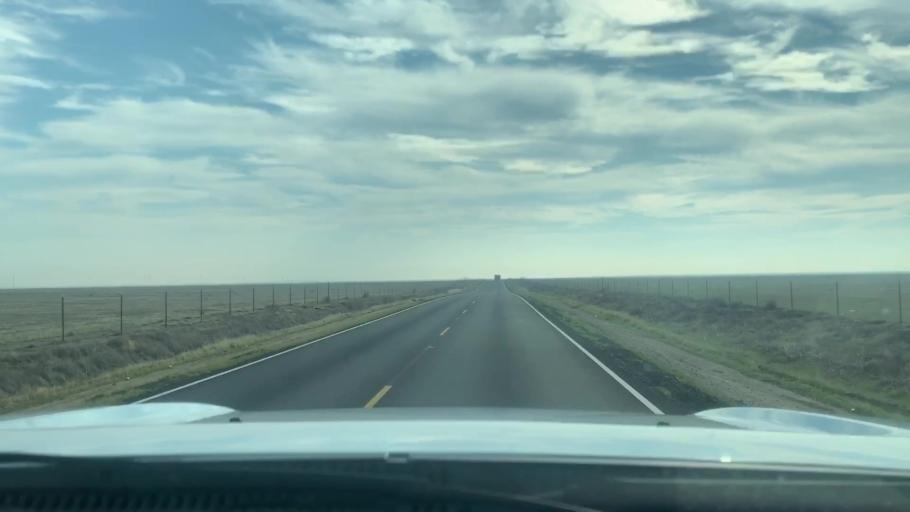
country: US
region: California
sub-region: Kern County
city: Lost Hills
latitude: 35.6064
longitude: -119.8573
